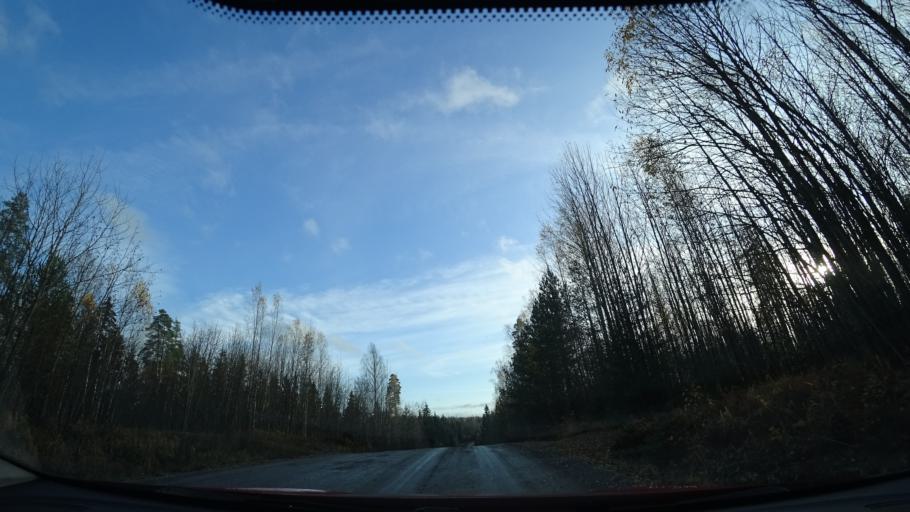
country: FI
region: Uusimaa
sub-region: Helsinki
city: Sibbo
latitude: 60.2985
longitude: 25.1994
